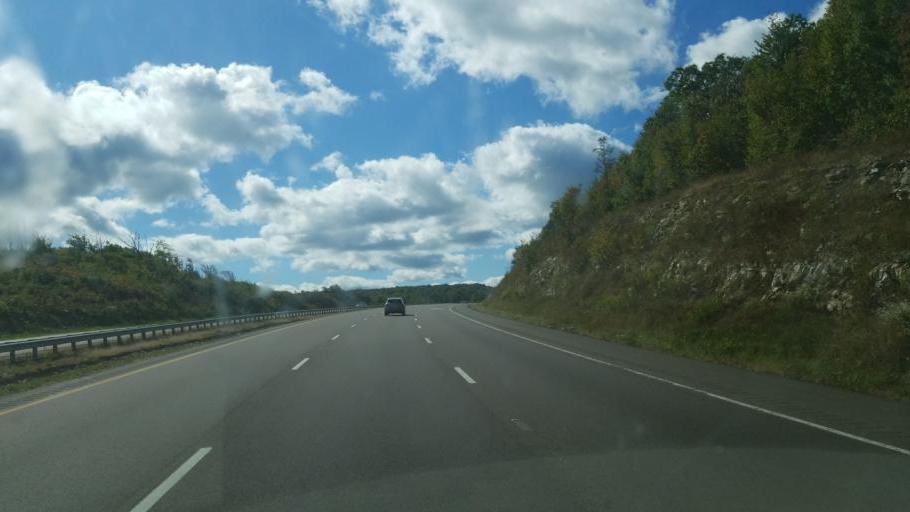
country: US
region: Pennsylvania
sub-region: Somerset County
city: Meyersdale
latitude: 39.6808
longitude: -79.2143
